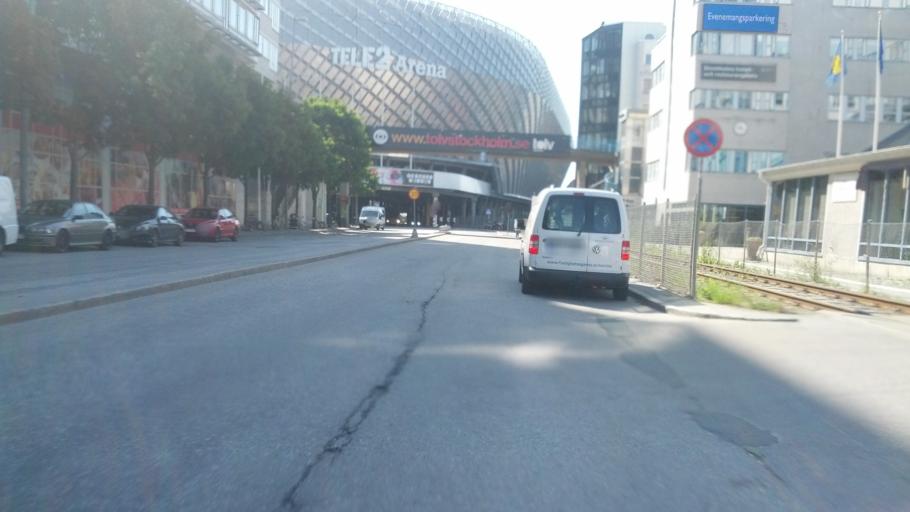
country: SE
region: Stockholm
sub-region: Stockholms Kommun
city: Arsta
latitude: 59.2927
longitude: 18.0809
